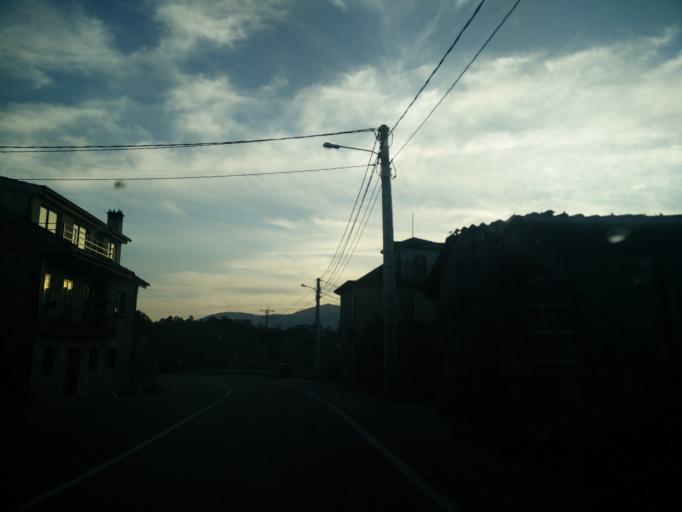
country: ES
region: Galicia
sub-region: Provincia de Pontevedra
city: Mondariz-Balneario
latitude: 42.2178
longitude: -8.4967
